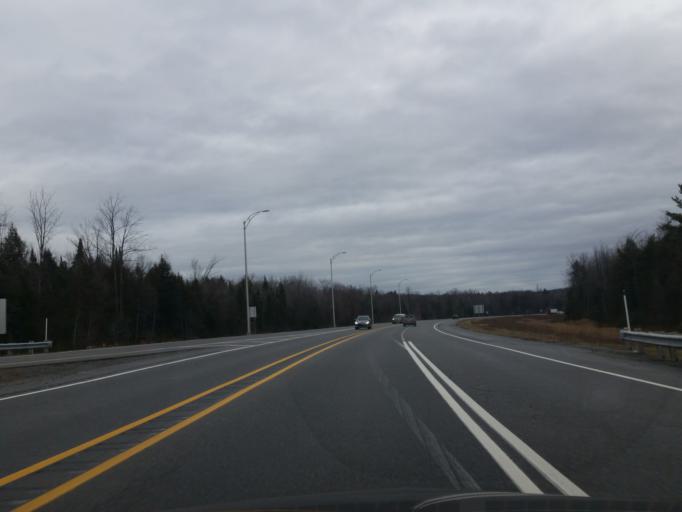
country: CA
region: Ontario
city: Clarence-Rockland
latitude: 45.6121
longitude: -75.3865
